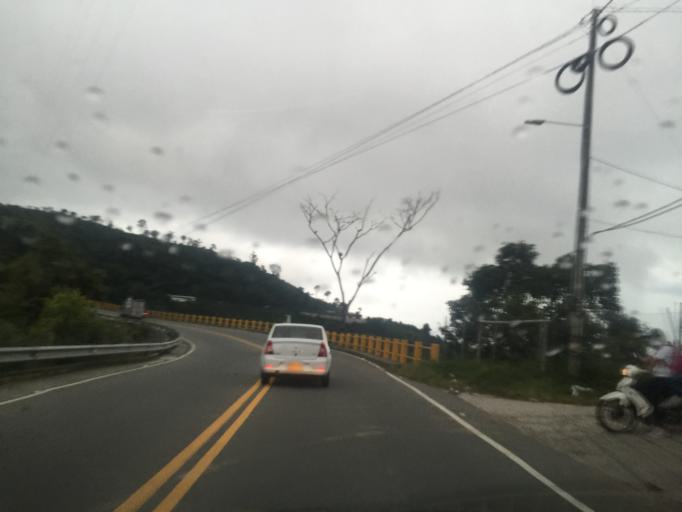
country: CO
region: Caldas
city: Villamaria
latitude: 5.0114
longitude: -75.5538
